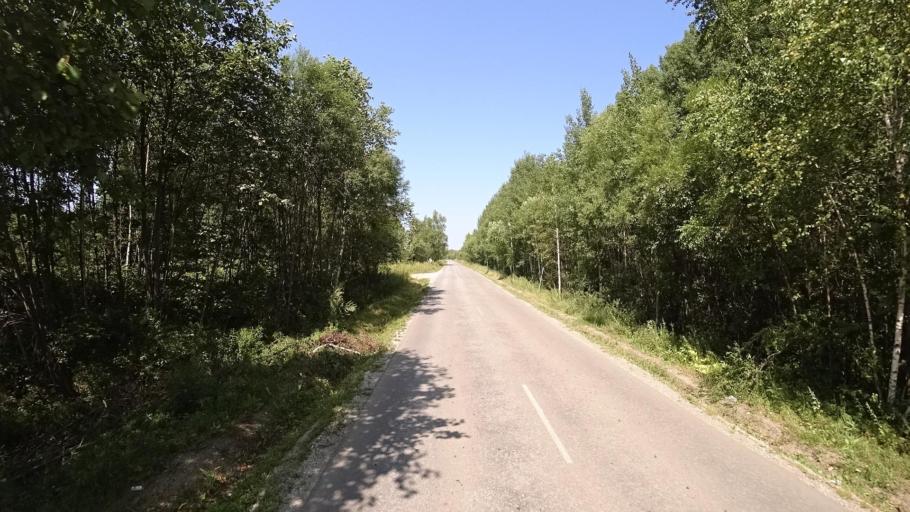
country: RU
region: Khabarovsk Krai
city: Khor
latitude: 47.9728
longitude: 135.1149
